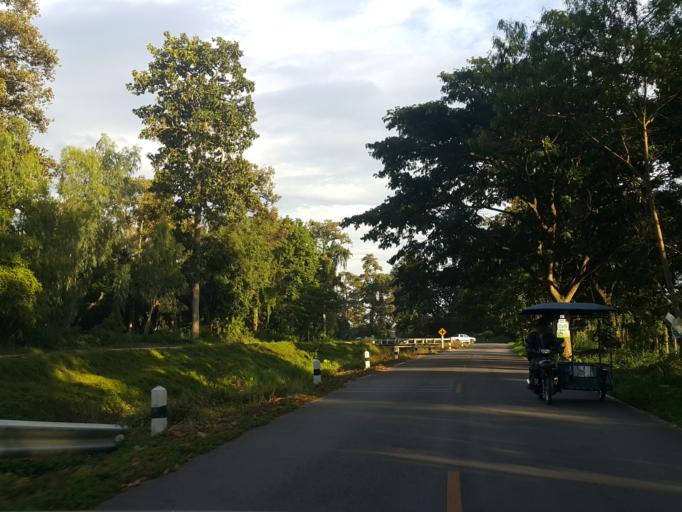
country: TH
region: Chiang Mai
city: San Sai
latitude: 18.8944
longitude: 99.0266
